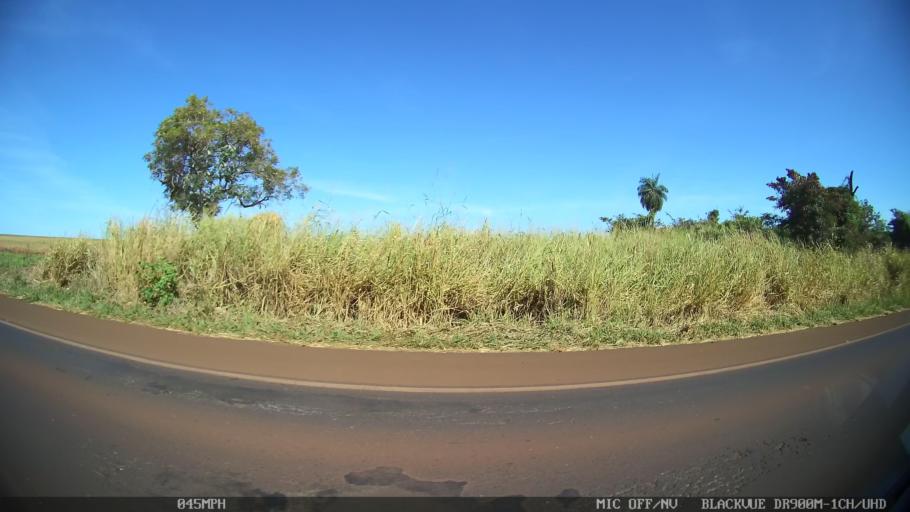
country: BR
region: Sao Paulo
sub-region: Sao Joaquim Da Barra
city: Sao Joaquim da Barra
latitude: -20.5060
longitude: -47.9291
